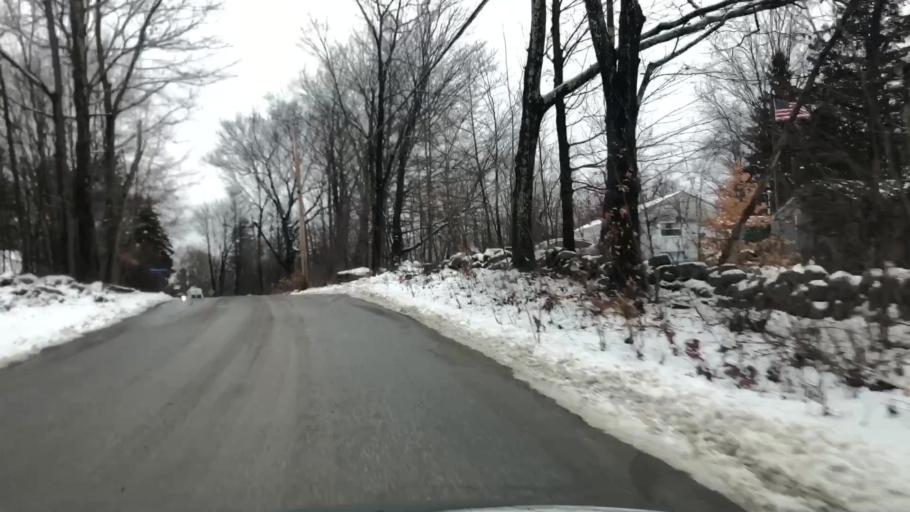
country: US
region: New Hampshire
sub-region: Hillsborough County
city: New Boston
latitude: 43.0127
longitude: -71.6819
